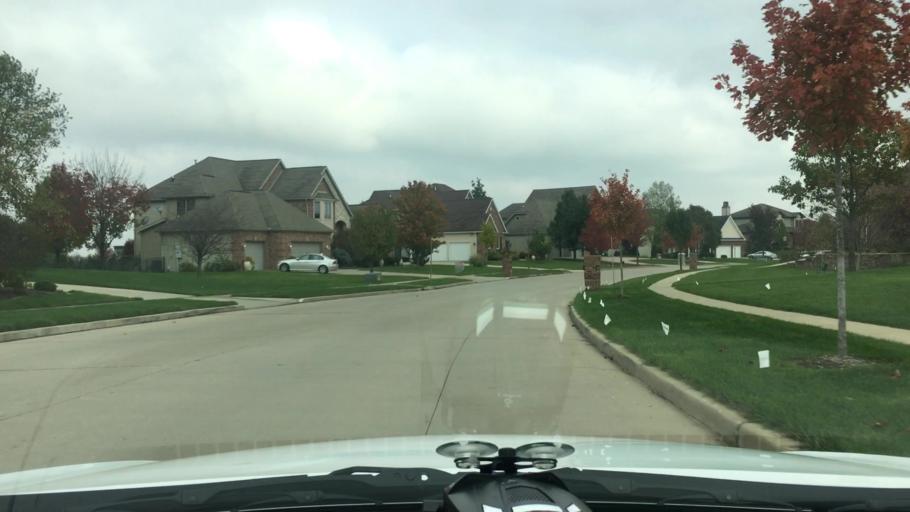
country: US
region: Illinois
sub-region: Champaign County
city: Champaign
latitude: 40.0962
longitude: -88.3228
